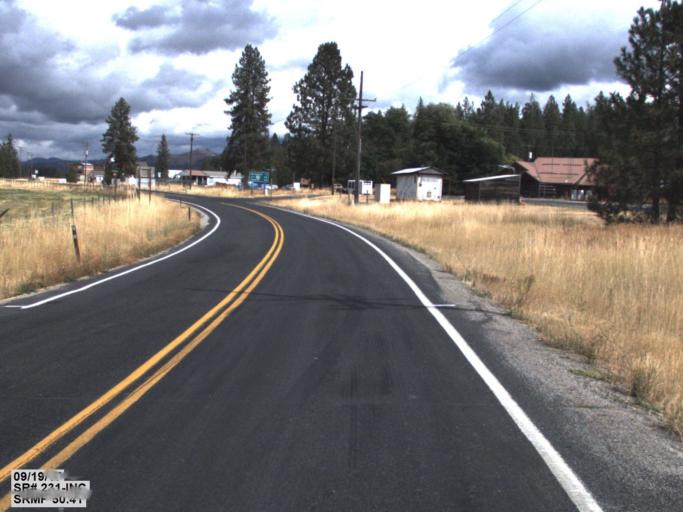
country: US
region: Washington
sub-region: Spokane County
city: Fairchild Air Force Base
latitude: 47.9085
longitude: -117.8063
